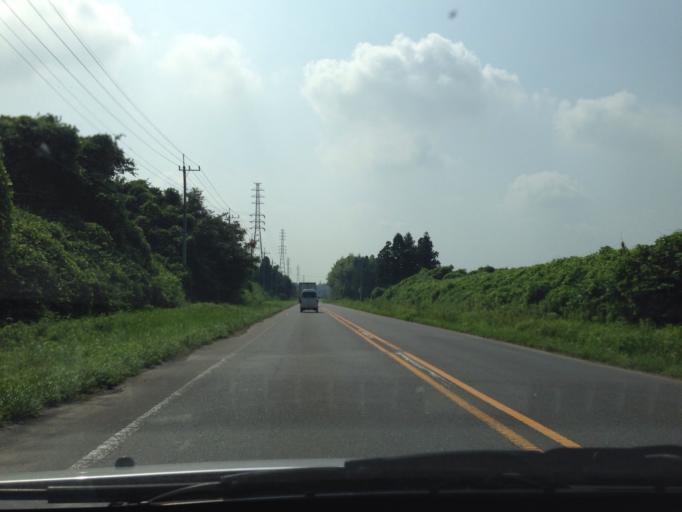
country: JP
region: Ibaraki
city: Ami
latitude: 36.0294
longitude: 140.2306
